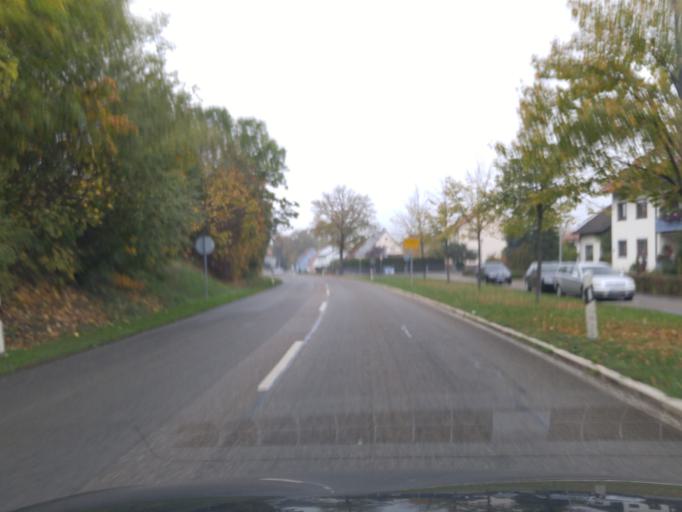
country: DE
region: Baden-Wuerttemberg
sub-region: Regierungsbezirk Stuttgart
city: Bad Rappenau
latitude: 49.2352
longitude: 9.1098
